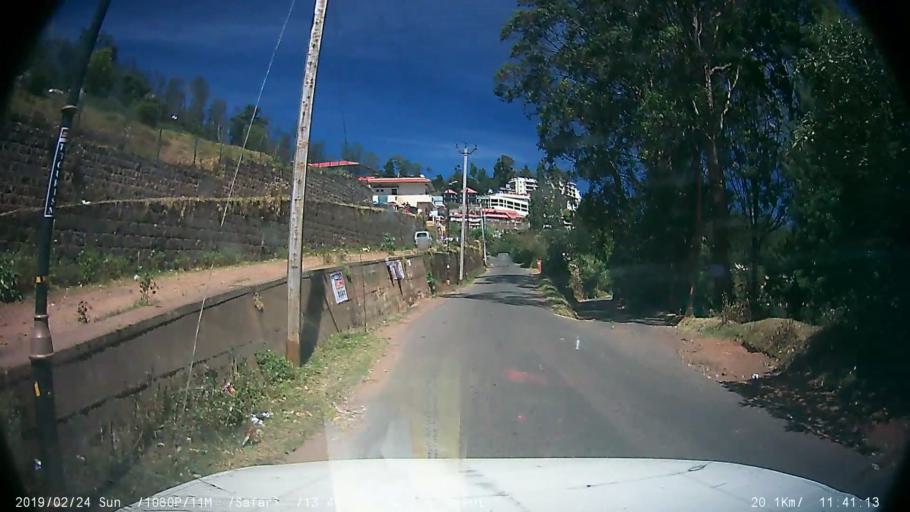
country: IN
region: Tamil Nadu
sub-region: Nilgiri
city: Ooty
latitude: 11.4172
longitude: 76.7050
